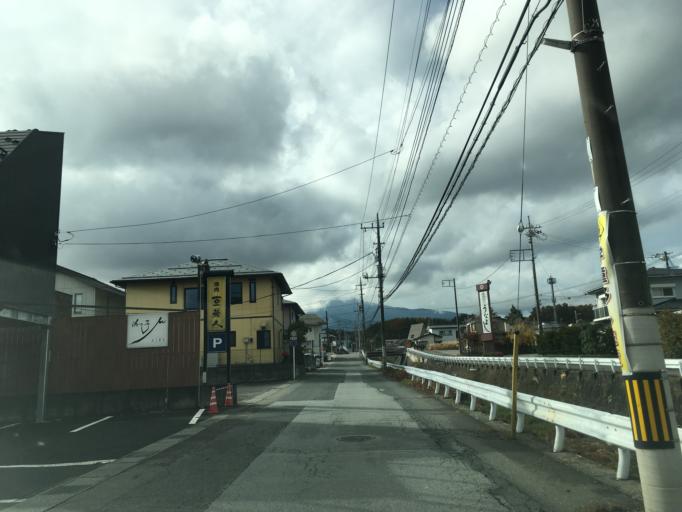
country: JP
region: Yamanashi
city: Fujikawaguchiko
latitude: 35.4844
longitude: 138.7825
